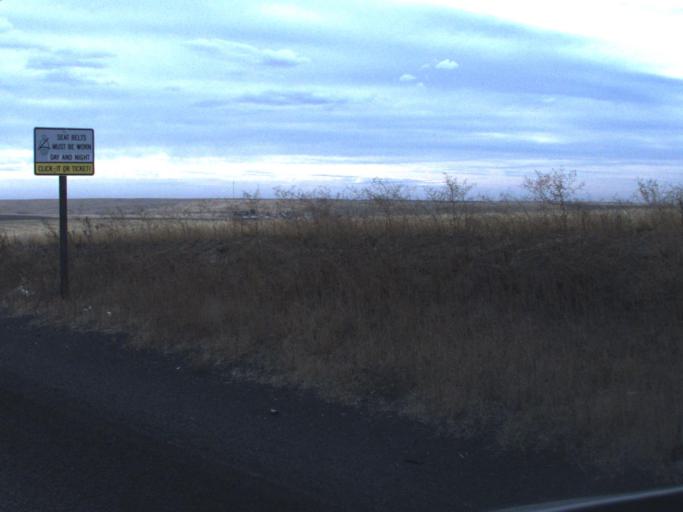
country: US
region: Washington
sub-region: Okanogan County
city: Coulee Dam
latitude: 47.8370
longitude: -118.7992
